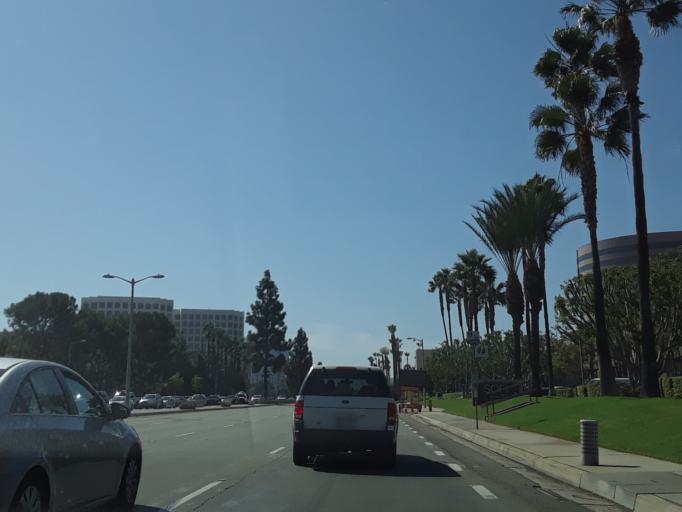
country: US
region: California
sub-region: Orange County
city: Irvine
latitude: 33.6836
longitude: -117.8372
